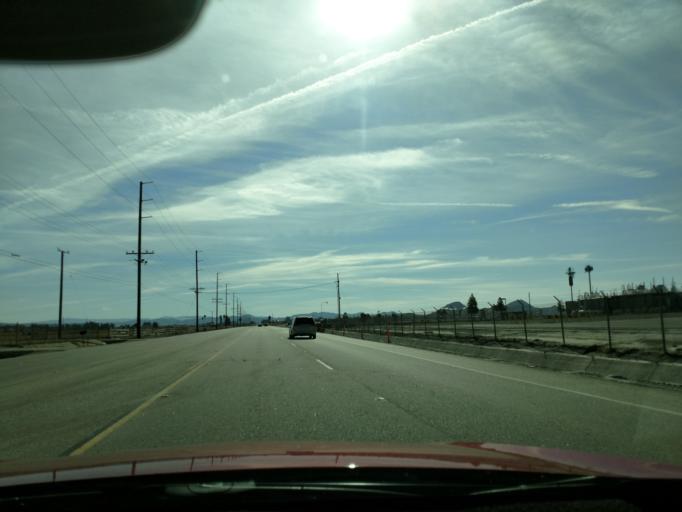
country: US
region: California
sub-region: Riverside County
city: San Jacinto
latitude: 33.7997
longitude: -117.0069
